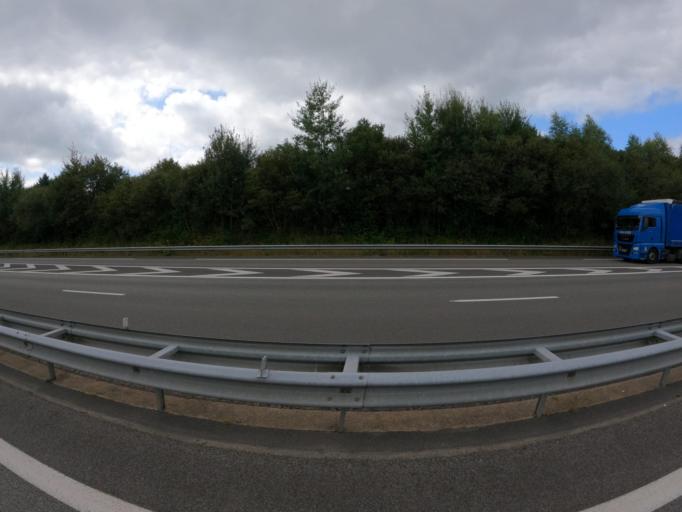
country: FR
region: Limousin
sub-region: Departement de la Haute-Vienne
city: Saint-Junien
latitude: 45.9055
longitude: 0.9315
